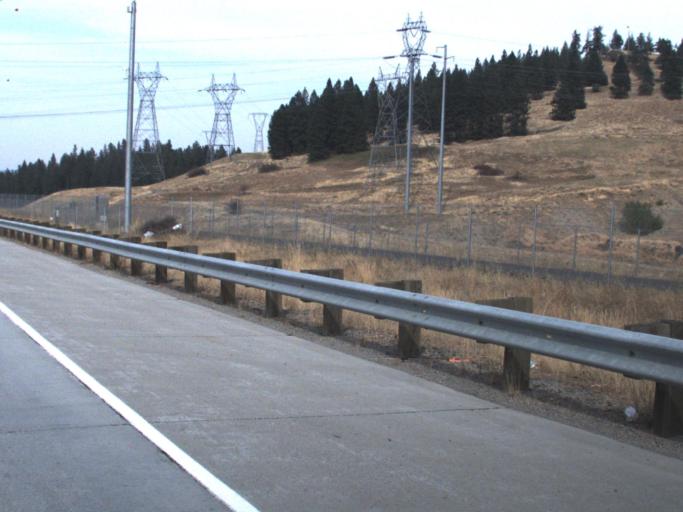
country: US
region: Washington
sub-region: Spokane County
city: Mead
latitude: 47.7493
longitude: -117.3593
